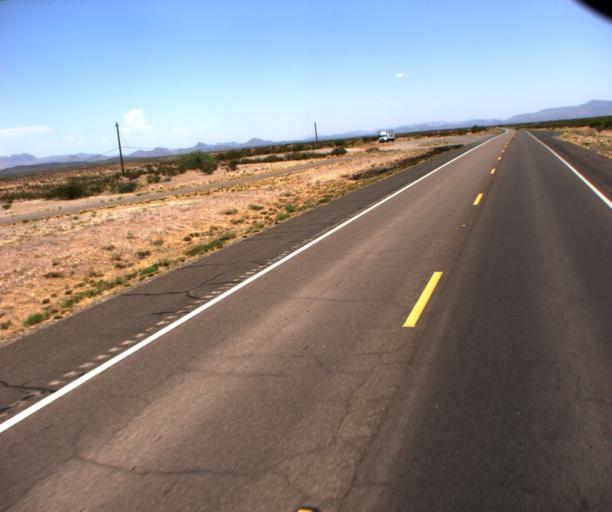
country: US
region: Arizona
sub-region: Graham County
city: Safford
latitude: 32.8087
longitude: -109.5854
